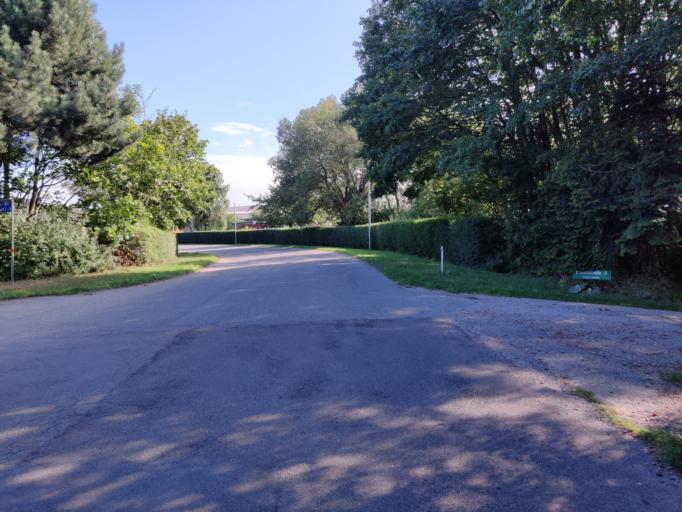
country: DK
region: Zealand
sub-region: Guldborgsund Kommune
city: Nykobing Falster
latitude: 54.7205
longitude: 11.9270
